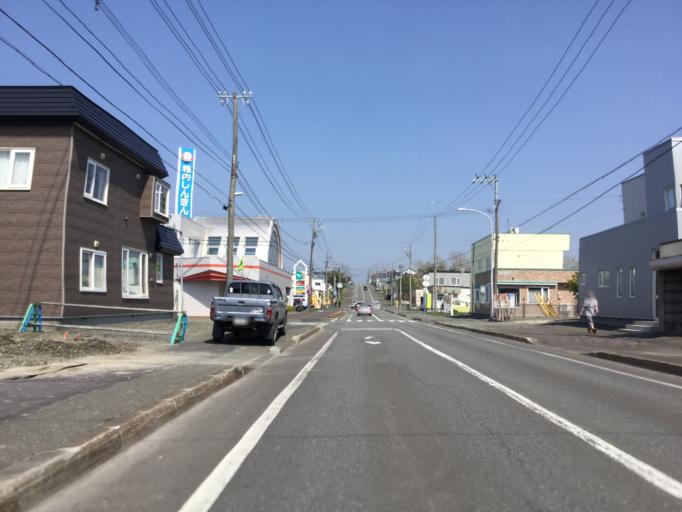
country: JP
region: Hokkaido
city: Wakkanai
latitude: 45.3894
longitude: 141.7155
